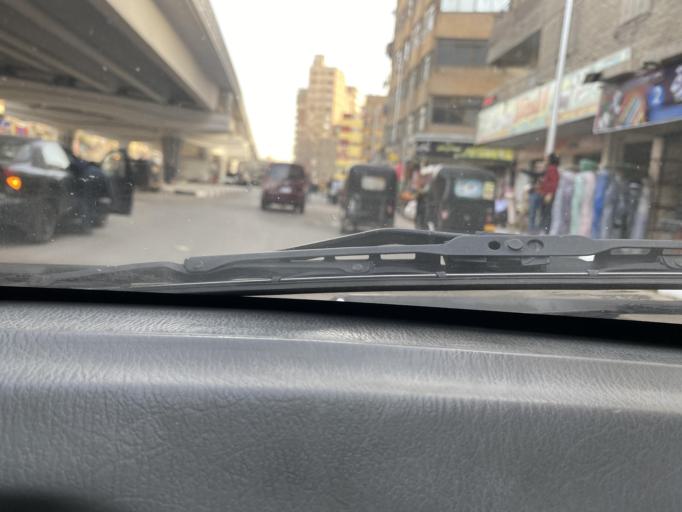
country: EG
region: Muhafazat al Qahirah
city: Cairo
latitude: 30.1215
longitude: 31.2970
